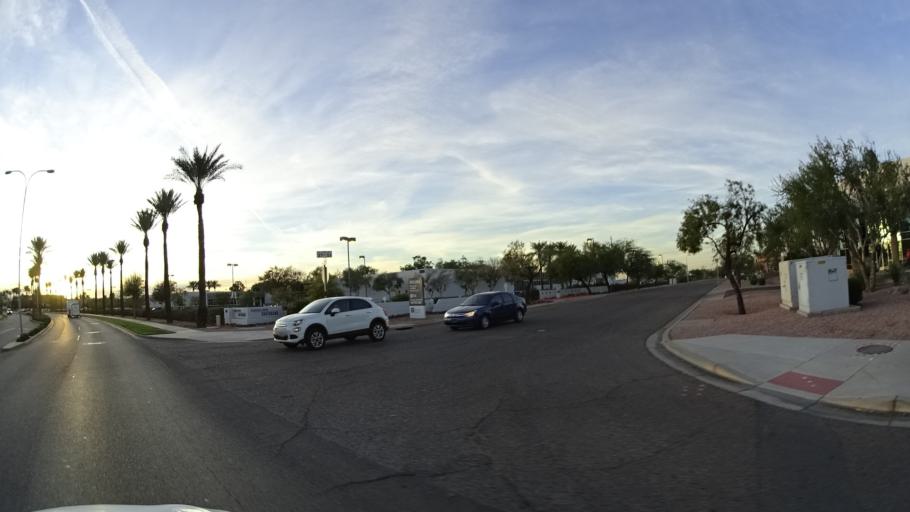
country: US
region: Arizona
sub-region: Maricopa County
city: Tempe Junction
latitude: 33.4219
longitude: -112.0013
